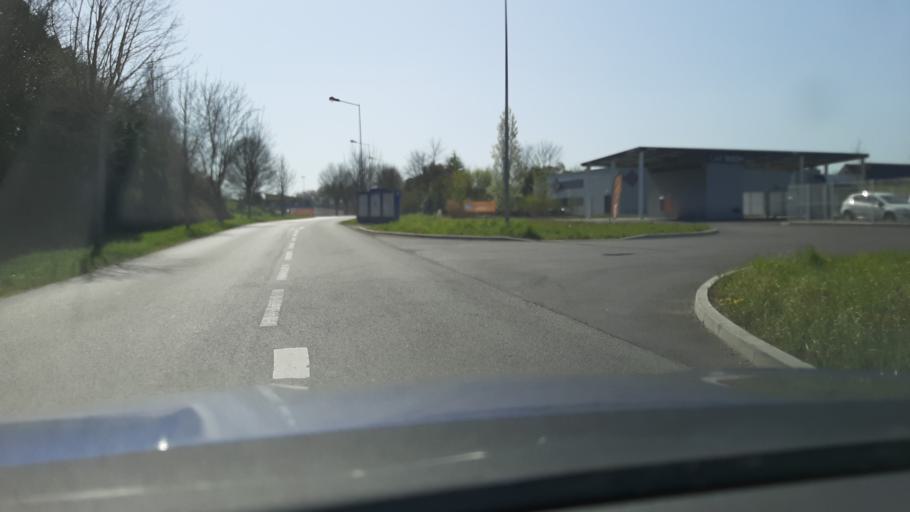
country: FR
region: Pays de la Loire
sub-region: Departement de Maine-et-Loire
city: Pellouailles-les-Vignes
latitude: 47.5232
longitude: -0.4302
